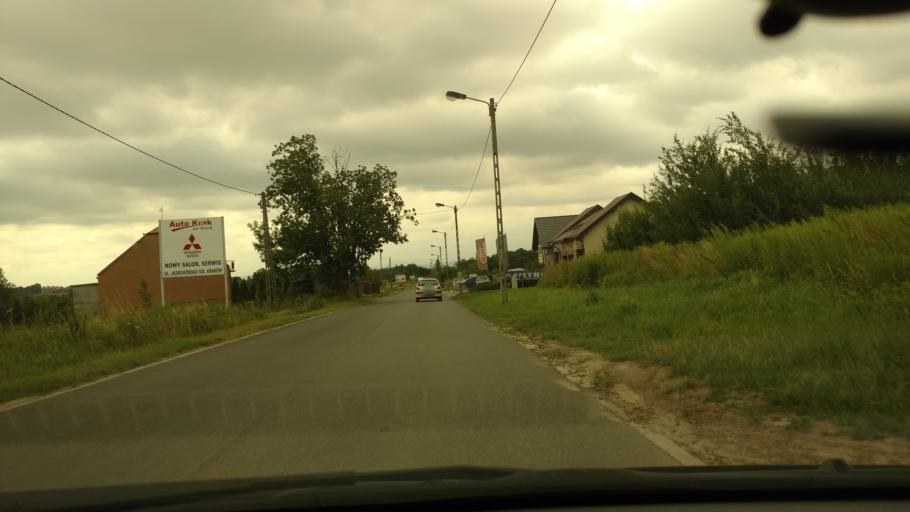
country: PL
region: Lesser Poland Voivodeship
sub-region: Powiat krakowski
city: Zielonki
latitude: 50.1166
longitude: 19.9421
